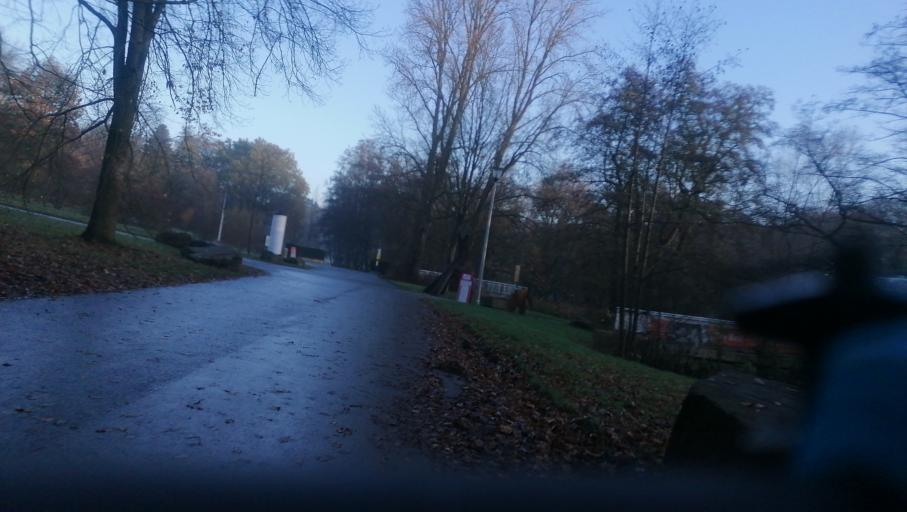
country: DE
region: North Rhine-Westphalia
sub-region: Regierungsbezirk Arnsberg
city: Dortmund
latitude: 51.4741
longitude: 7.4670
